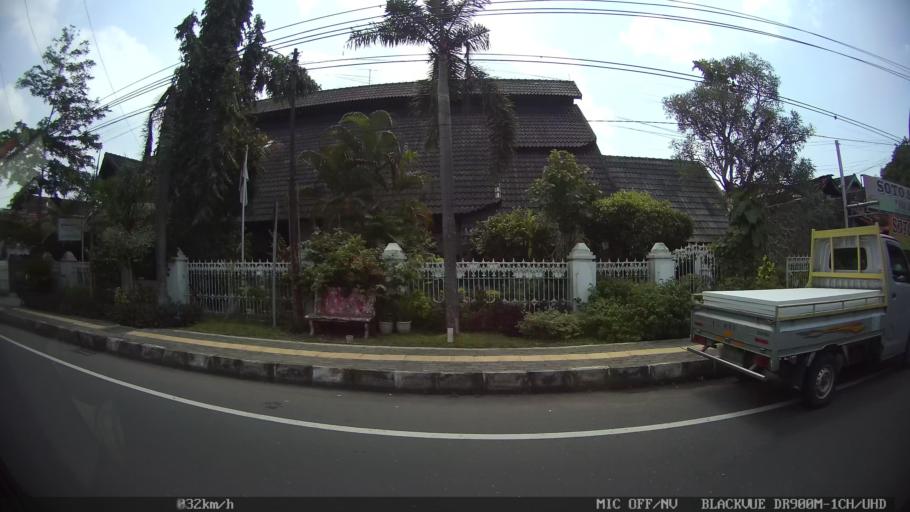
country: ID
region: Daerah Istimewa Yogyakarta
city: Yogyakarta
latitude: -7.8101
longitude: 110.3970
